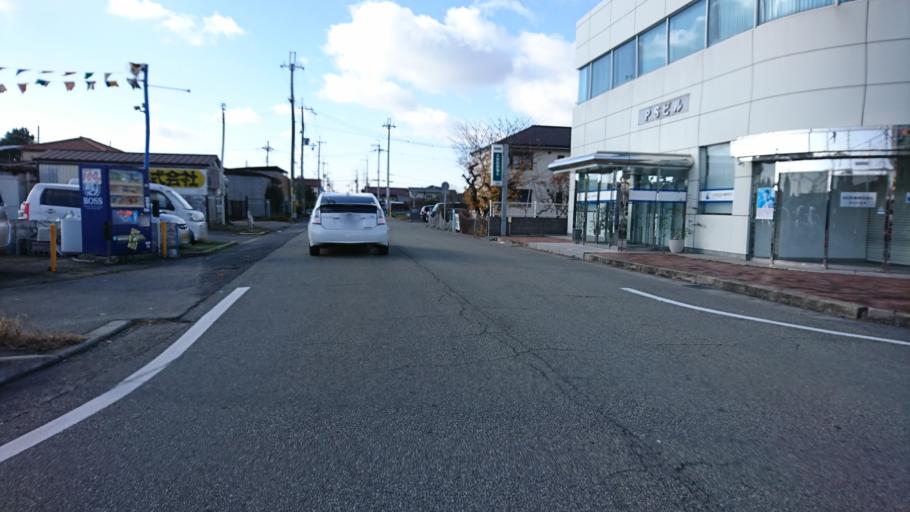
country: JP
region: Hyogo
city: Kakogawacho-honmachi
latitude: 34.7506
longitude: 134.8171
